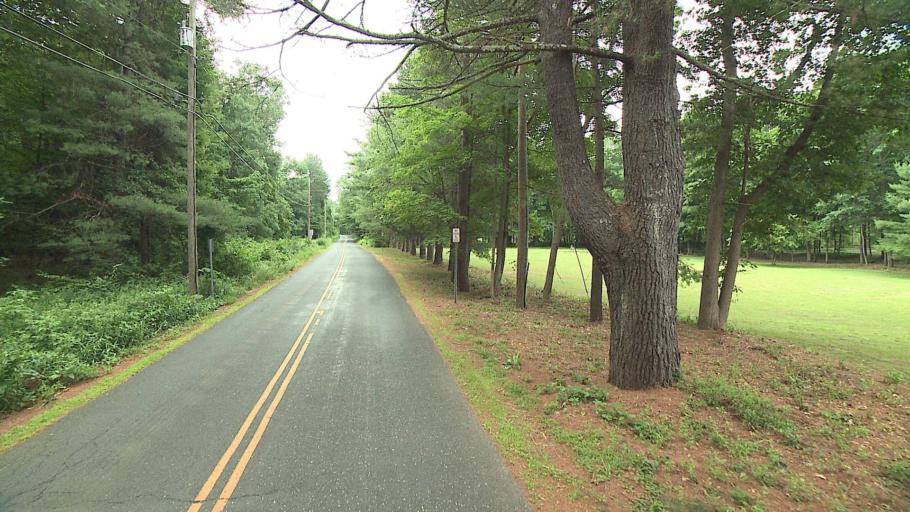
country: US
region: Connecticut
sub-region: Litchfield County
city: New Hartford Center
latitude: 41.9213
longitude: -72.9937
